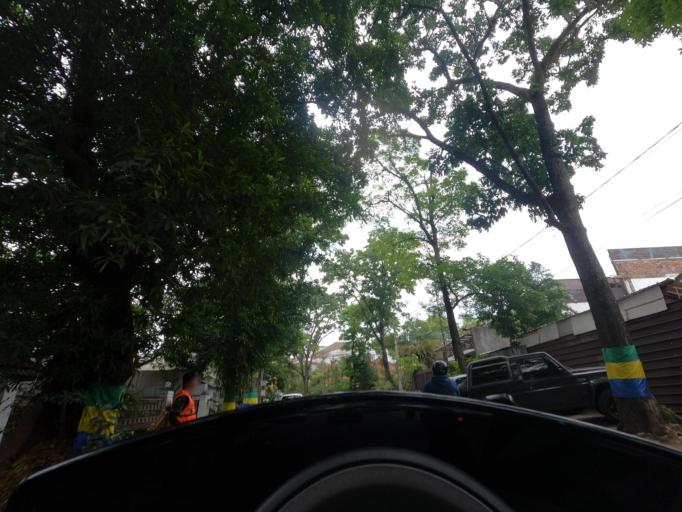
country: ID
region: West Java
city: Bandung
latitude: -6.9087
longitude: 107.6264
